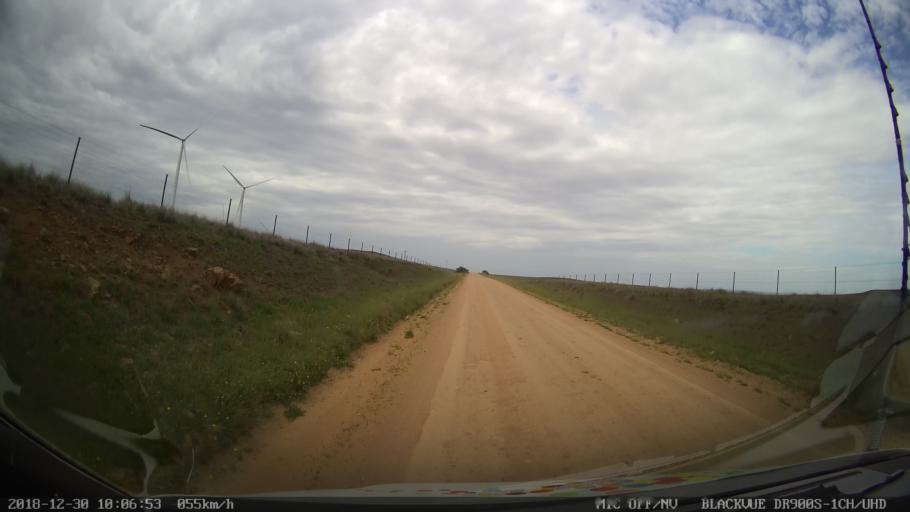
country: AU
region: New South Wales
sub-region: Cooma-Monaro
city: Cooma
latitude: -36.5356
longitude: 149.1267
